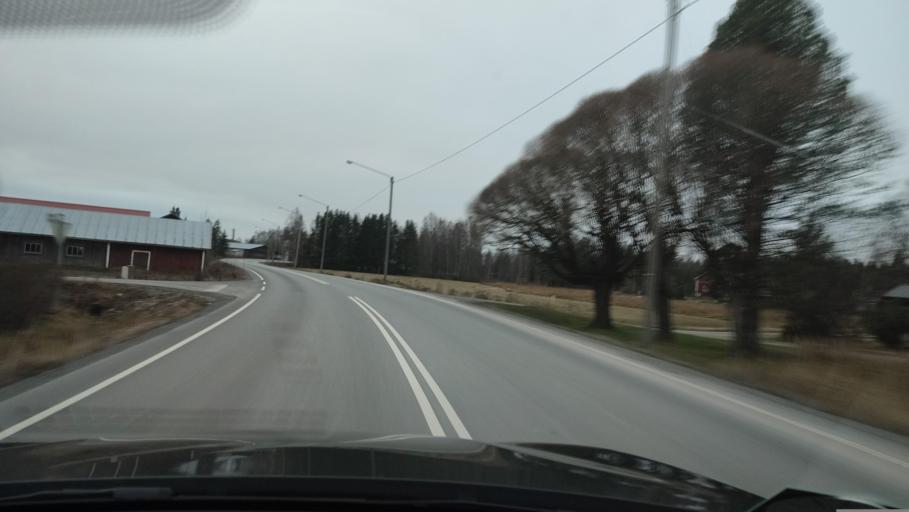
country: FI
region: Ostrobothnia
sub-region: Sydosterbotten
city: Kristinestad
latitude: 62.2654
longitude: 21.5422
